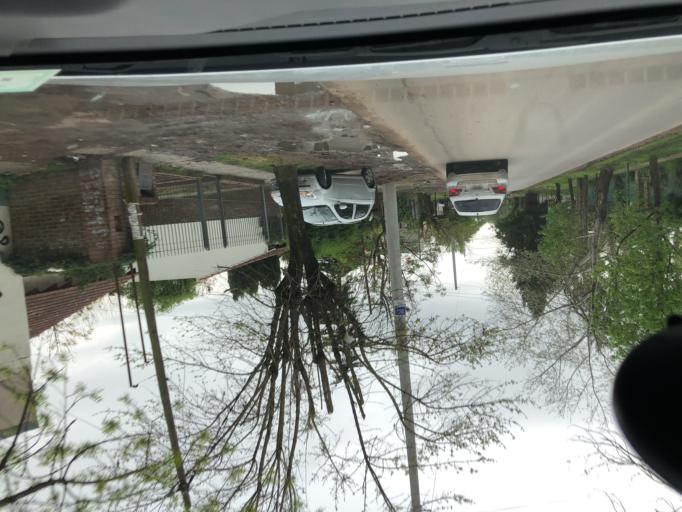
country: AR
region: Buenos Aires
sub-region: Partido de La Plata
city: La Plata
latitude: -34.8945
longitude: -58.0657
